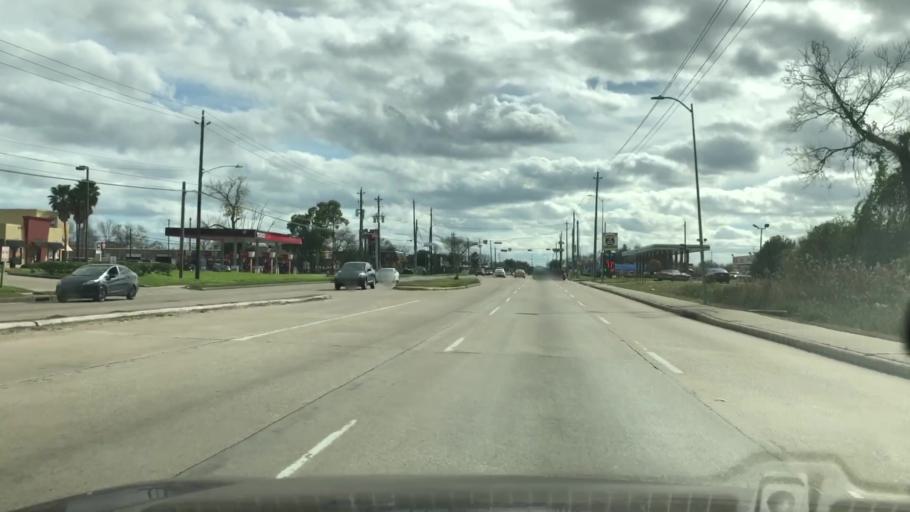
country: US
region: Texas
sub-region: Harris County
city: Bellaire
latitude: 29.6423
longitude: -95.4638
